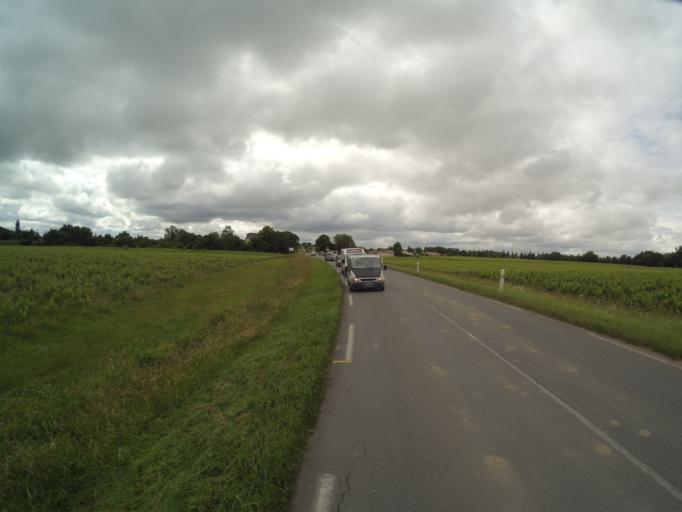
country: FR
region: Aquitaine
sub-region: Departement de la Gironde
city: Cantenac
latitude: 45.0274
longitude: -0.6476
